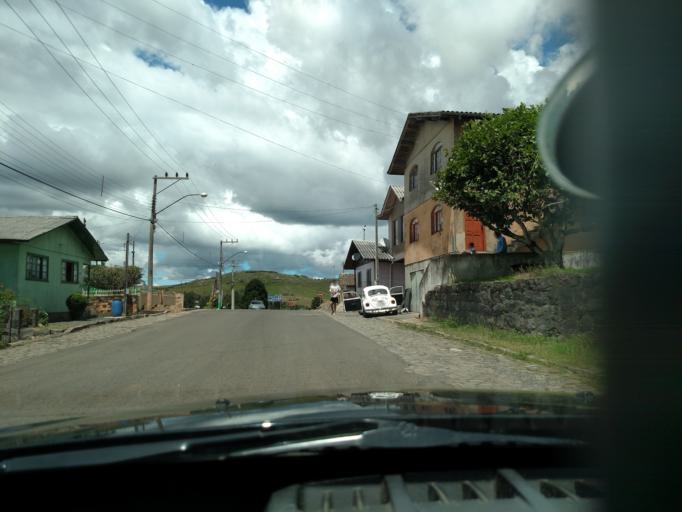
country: BR
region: Santa Catarina
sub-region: Sao Joaquim
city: Sao Joaquim
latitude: -28.2842
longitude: -49.9322
